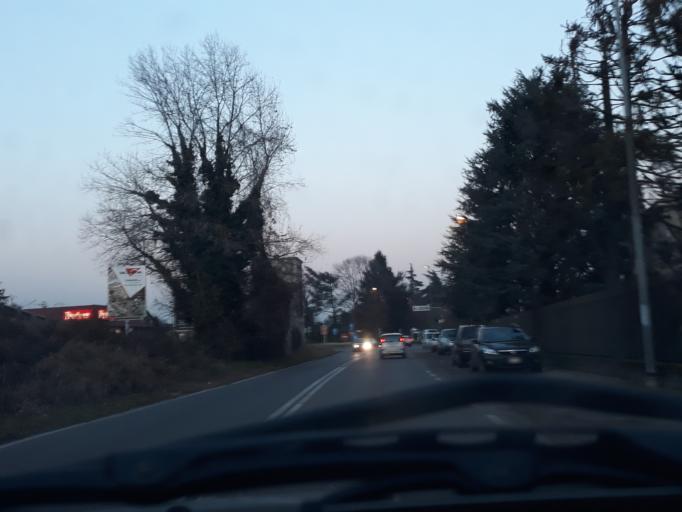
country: IT
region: Lombardy
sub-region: Provincia di Monza e Brianza
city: Lissone
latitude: 45.6068
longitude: 9.2271
